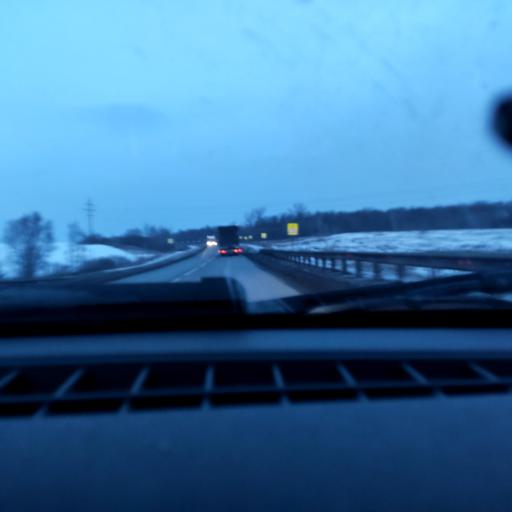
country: RU
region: Bashkortostan
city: Avdon
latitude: 54.7327
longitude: 55.7817
